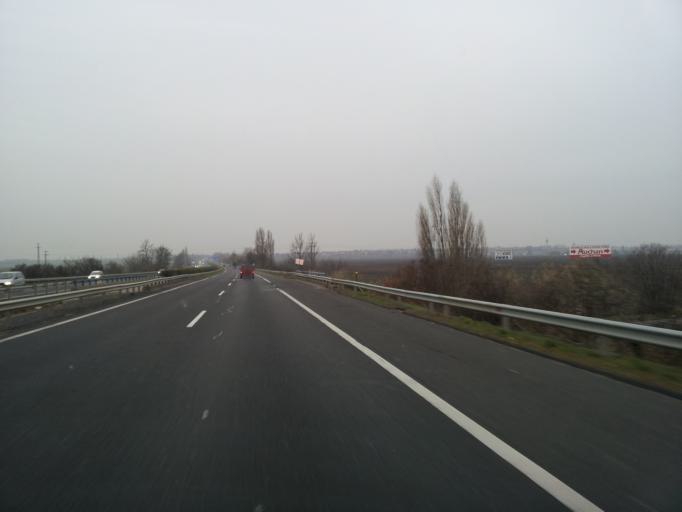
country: HU
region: Fejer
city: Szekesfehervar
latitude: 47.1662
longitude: 18.4577
